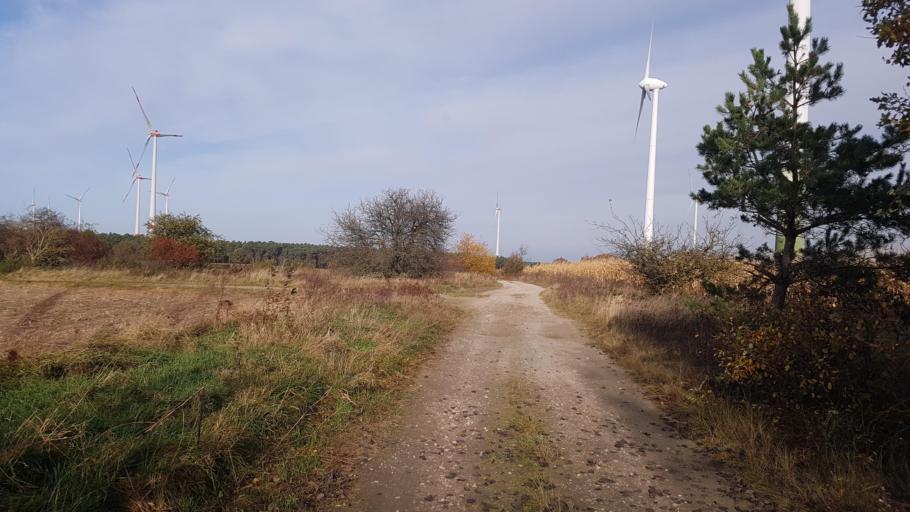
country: DE
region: Brandenburg
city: Treuenbrietzen
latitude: 52.0096
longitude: 12.8798
